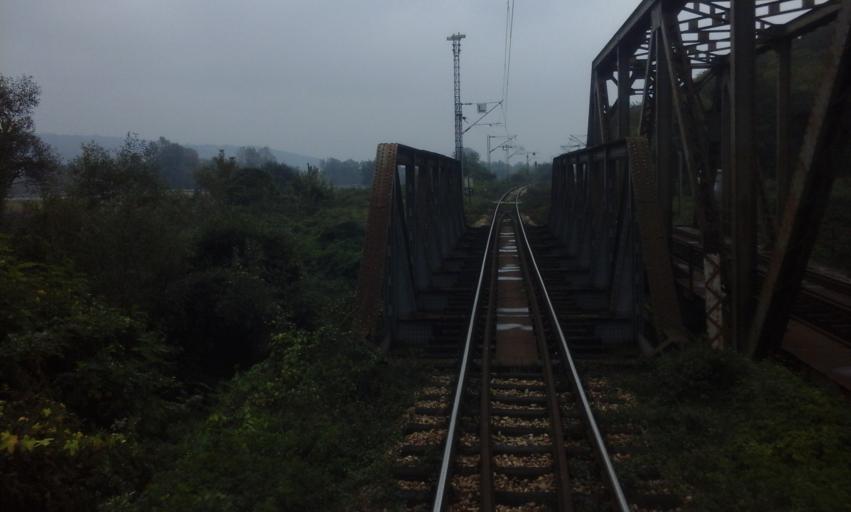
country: RS
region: Central Serbia
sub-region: Sumadijski Okrug
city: Batocina
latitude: 44.0802
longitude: 21.1853
